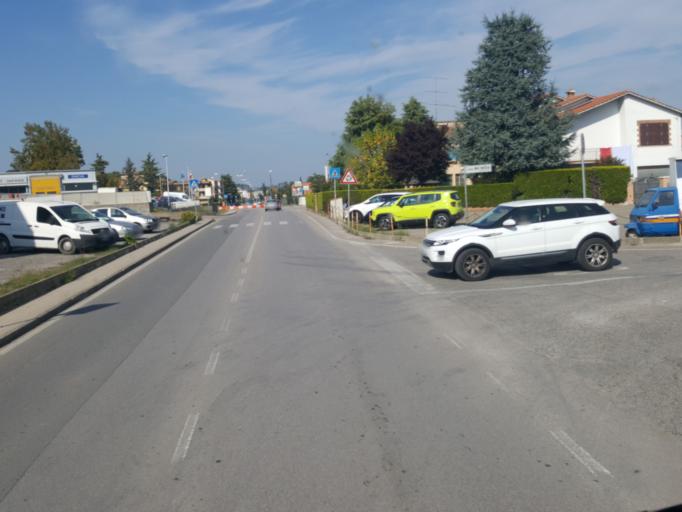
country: IT
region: Tuscany
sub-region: Provincia di Siena
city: Colle di Val d'Elsa
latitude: 43.4095
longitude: 11.1332
